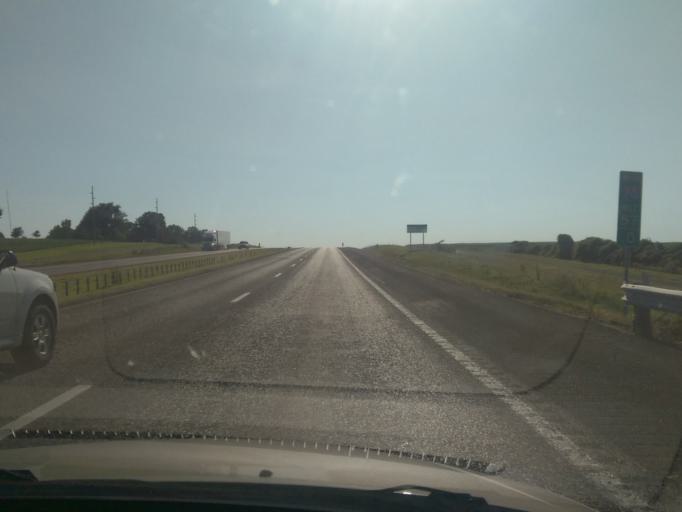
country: US
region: Missouri
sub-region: Lafayette County
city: Concordia
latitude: 38.9938
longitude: -93.5982
